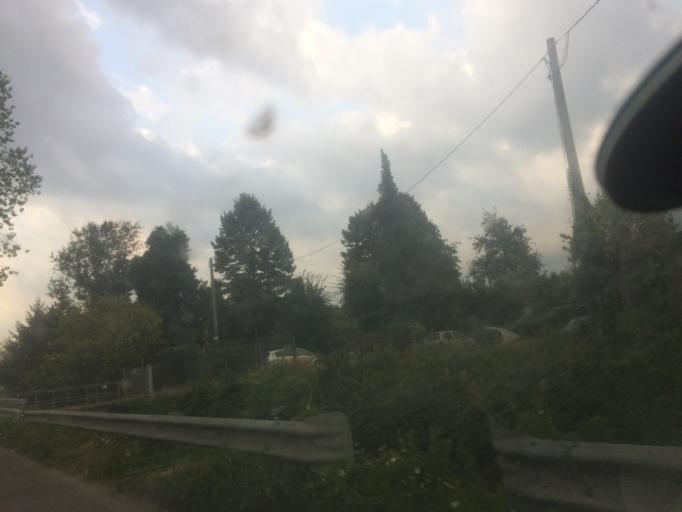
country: IT
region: Tuscany
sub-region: Provincia di Massa-Carrara
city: Massa
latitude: 44.0205
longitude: 10.0960
